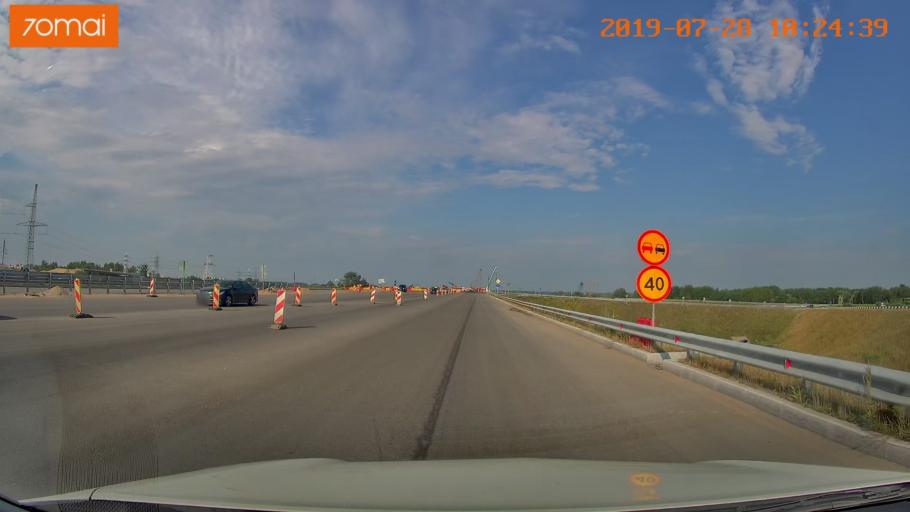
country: RU
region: Kaliningrad
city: Maloye Isakovo
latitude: 54.7683
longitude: 20.5493
